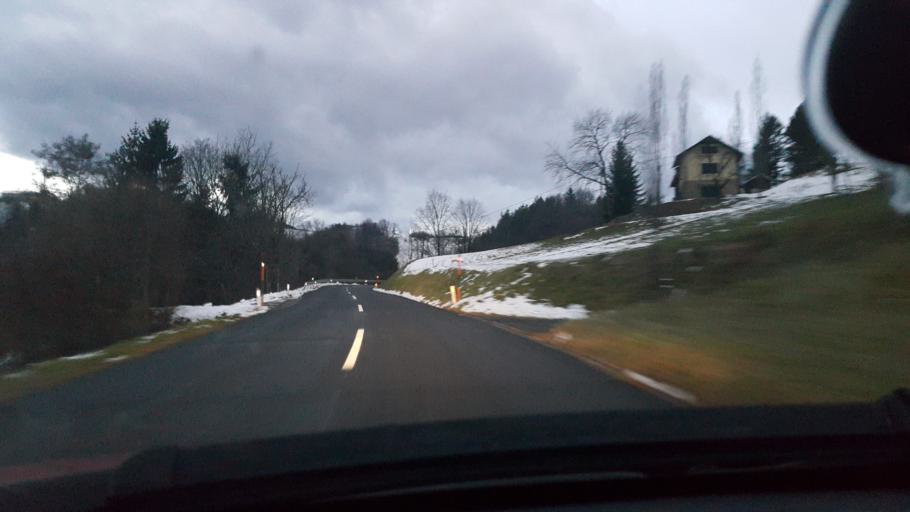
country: AT
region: Styria
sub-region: Politischer Bezirk Leibnitz
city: Sulztal an der Weinstrasse
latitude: 46.6467
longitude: 15.5244
